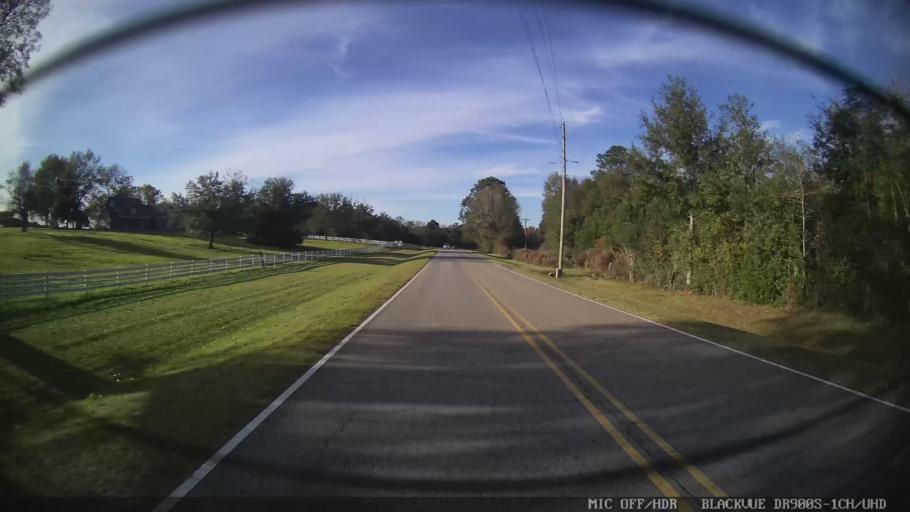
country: US
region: Mississippi
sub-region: Forrest County
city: Hattiesburg
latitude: 31.1967
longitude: -89.2904
